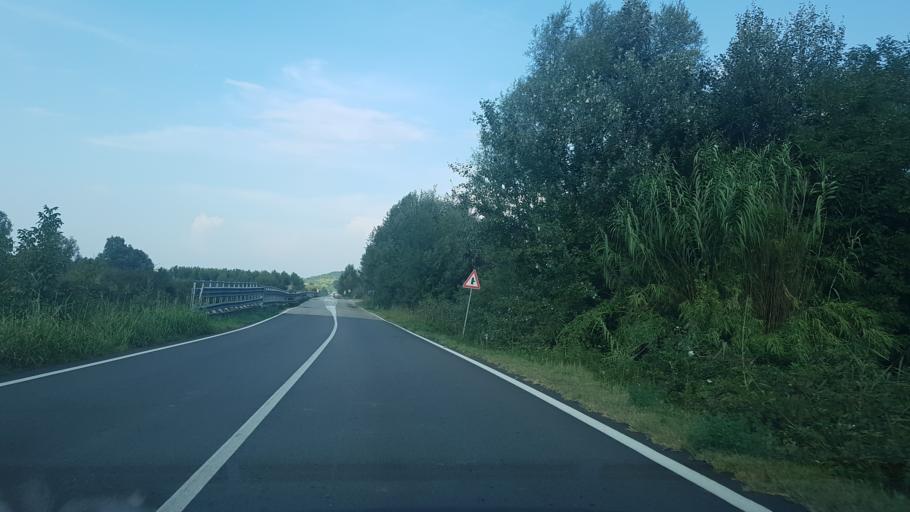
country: IT
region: Piedmont
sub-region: Provincia di Asti
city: Bruno
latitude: 44.8000
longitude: 8.4451
